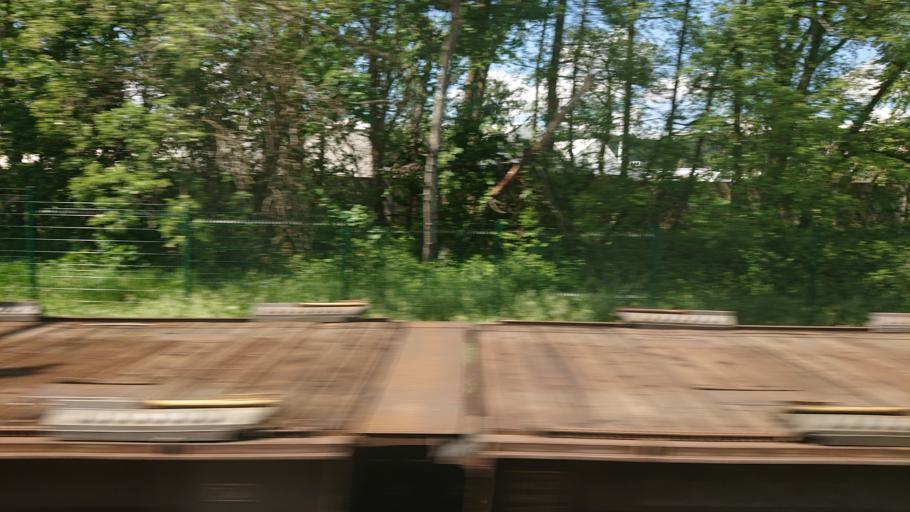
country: FR
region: Rhone-Alpes
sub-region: Departement de l'Ain
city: Montluel
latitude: 45.8447
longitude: 5.0512
